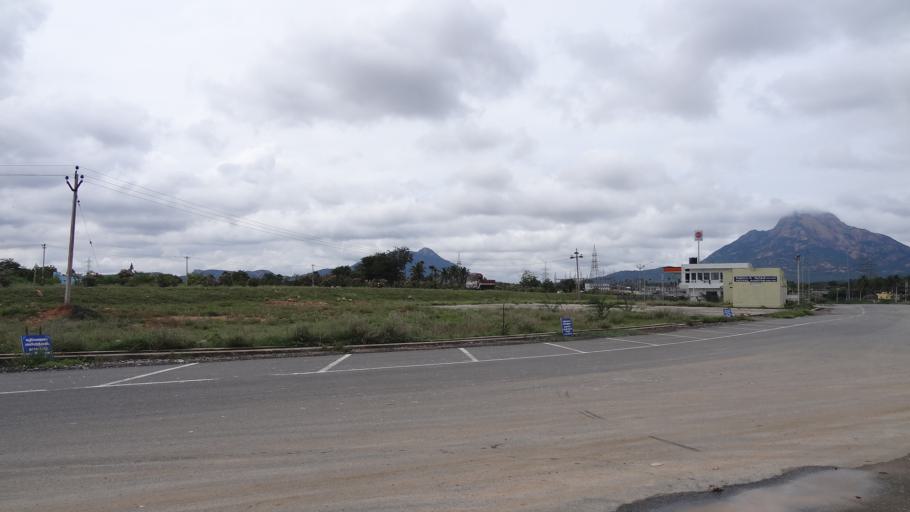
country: IN
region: Tamil Nadu
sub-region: Dindigul
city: Vedasandur
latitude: 10.5976
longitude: 77.9368
